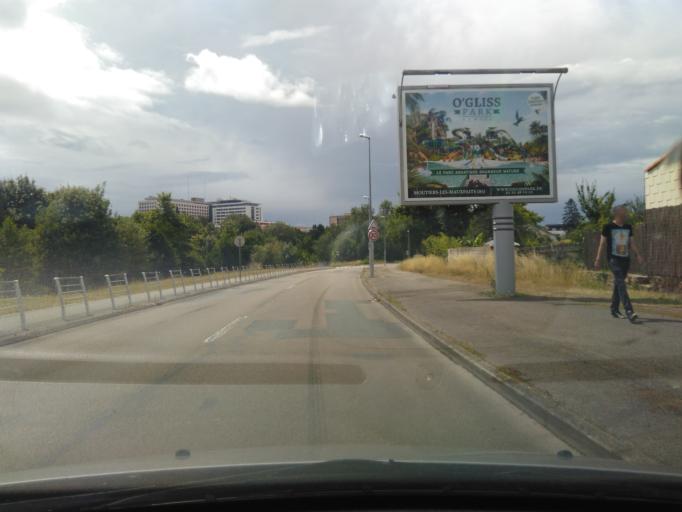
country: FR
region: Pays de la Loire
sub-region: Departement de la Vendee
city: La Roche-sur-Yon
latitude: 46.6733
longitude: -1.4155
